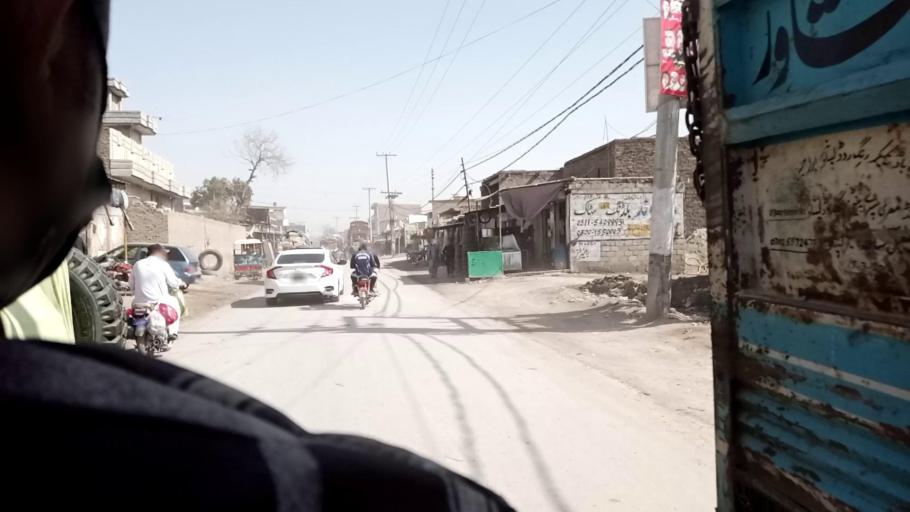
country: PK
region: Khyber Pakhtunkhwa
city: Peshawar
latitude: 34.0067
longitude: 71.6417
